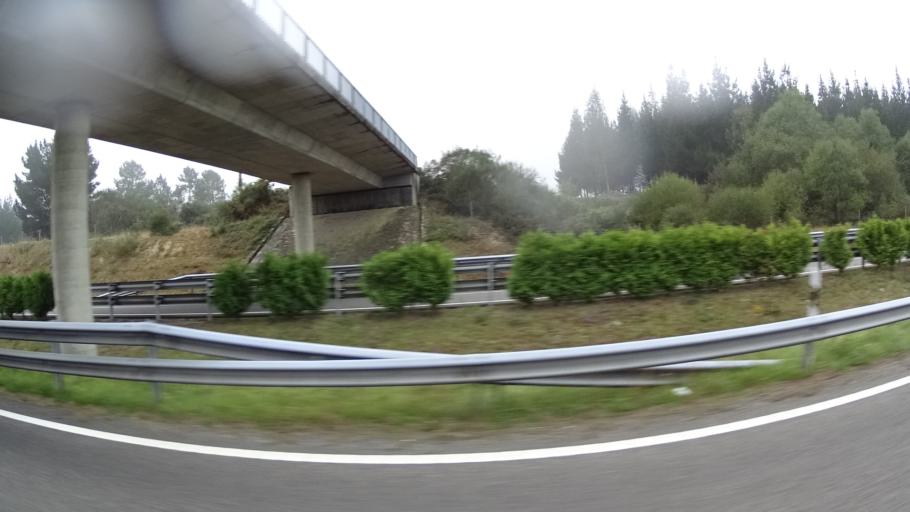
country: ES
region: Galicia
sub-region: Provincia de Lugo
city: Outeiro de Rei
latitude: 43.0920
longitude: -7.5877
